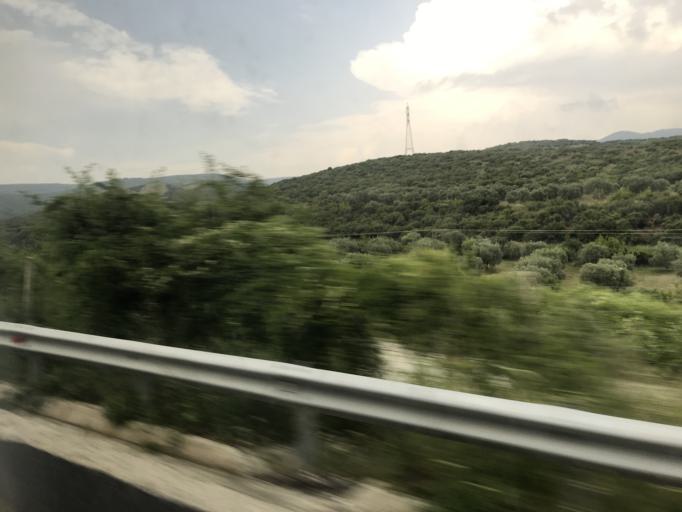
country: GR
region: East Macedonia and Thrace
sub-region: Nomos Rodopis
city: Sapes
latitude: 40.8759
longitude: 25.7109
